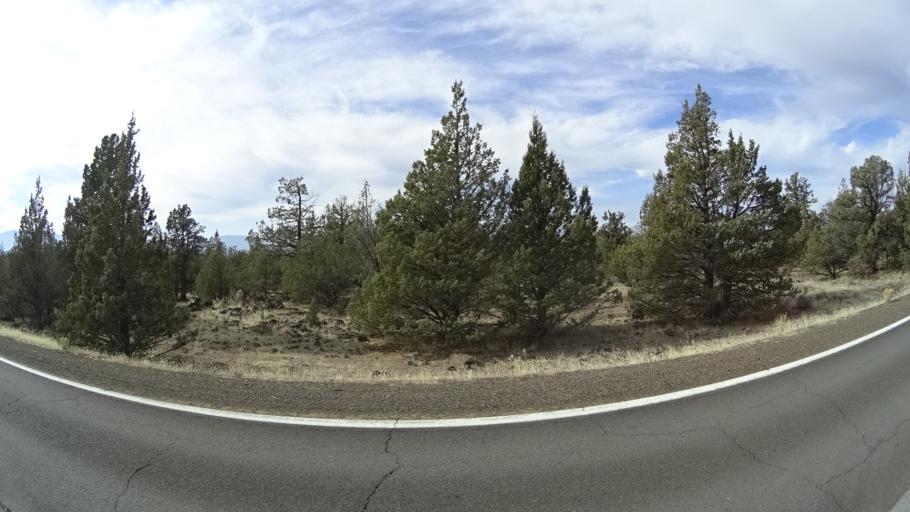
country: US
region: California
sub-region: Siskiyou County
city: Weed
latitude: 41.5977
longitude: -122.3954
